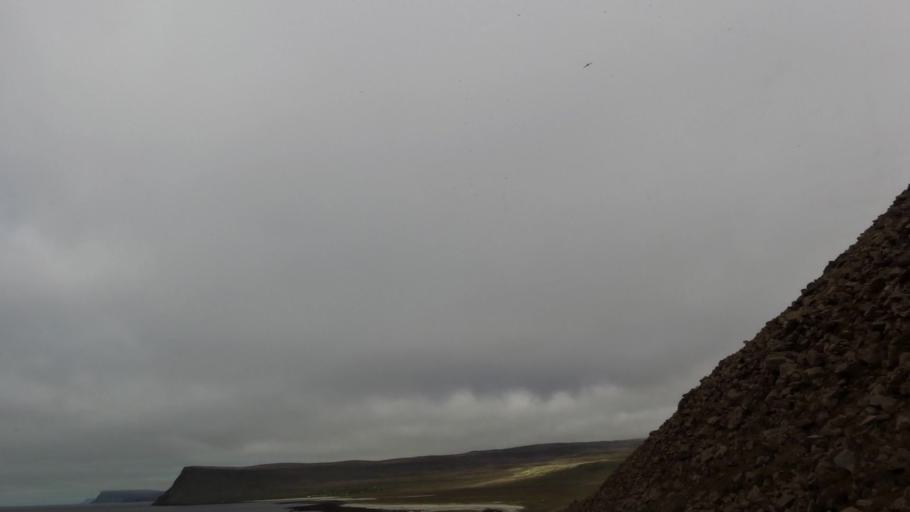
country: IS
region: West
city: Olafsvik
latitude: 65.5118
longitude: -24.5054
